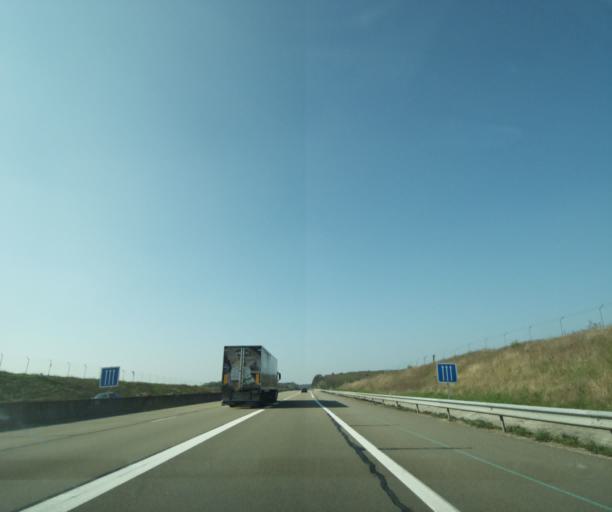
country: FR
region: Ile-de-France
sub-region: Departement de Seine-et-Marne
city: Souppes-sur-Loing
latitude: 48.2276
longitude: 2.7618
